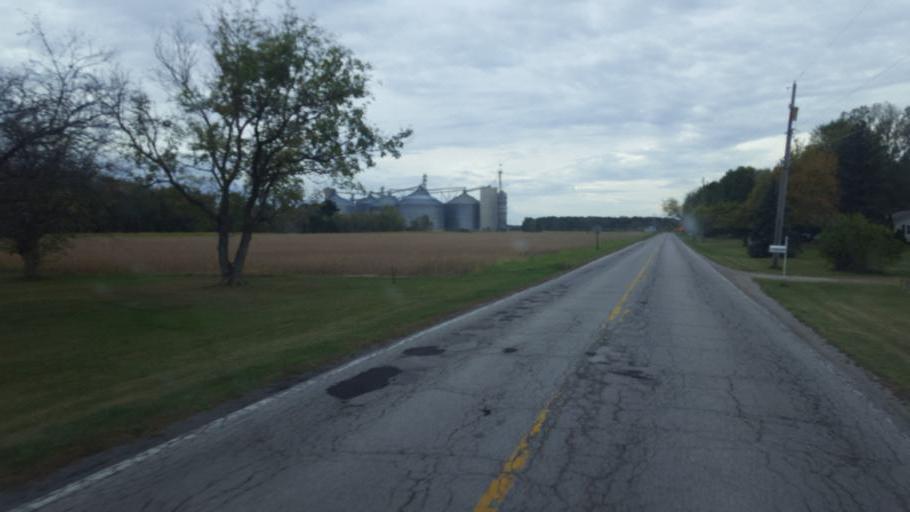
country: US
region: Ohio
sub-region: Huron County
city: Wakeman
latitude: 41.1961
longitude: -82.4220
